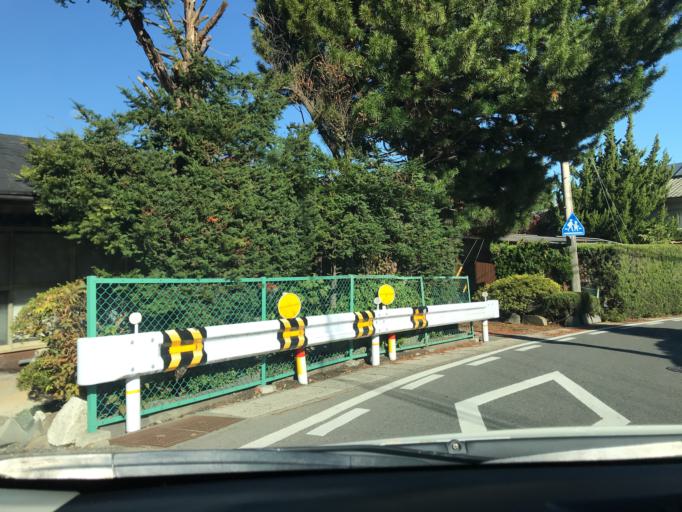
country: JP
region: Nagano
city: Matsumoto
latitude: 36.1880
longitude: 137.8549
